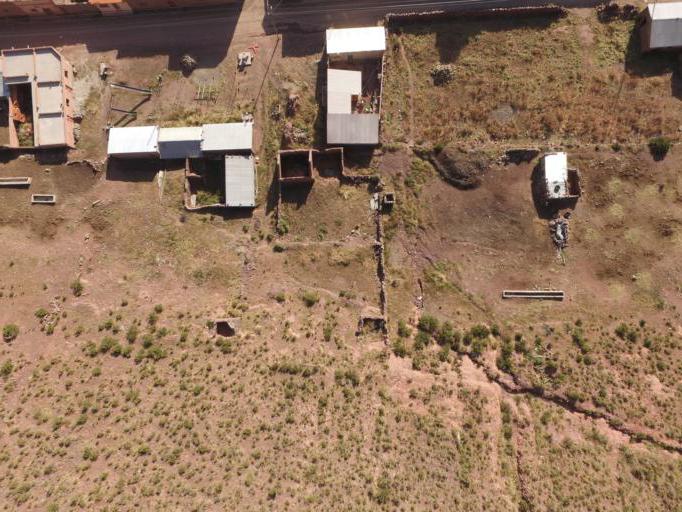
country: BO
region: Oruro
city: Challapata
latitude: -18.6936
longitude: -66.7562
